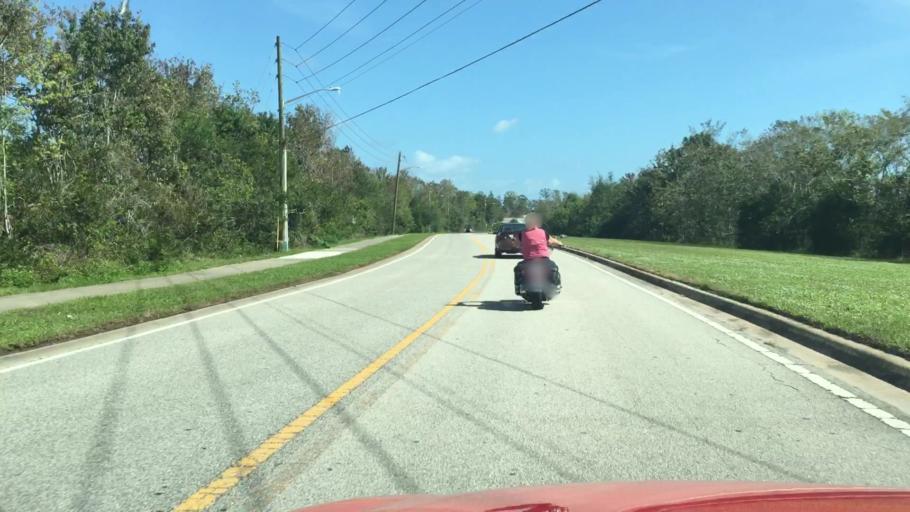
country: US
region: Florida
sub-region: Volusia County
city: South Daytona
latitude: 29.1420
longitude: -81.0414
